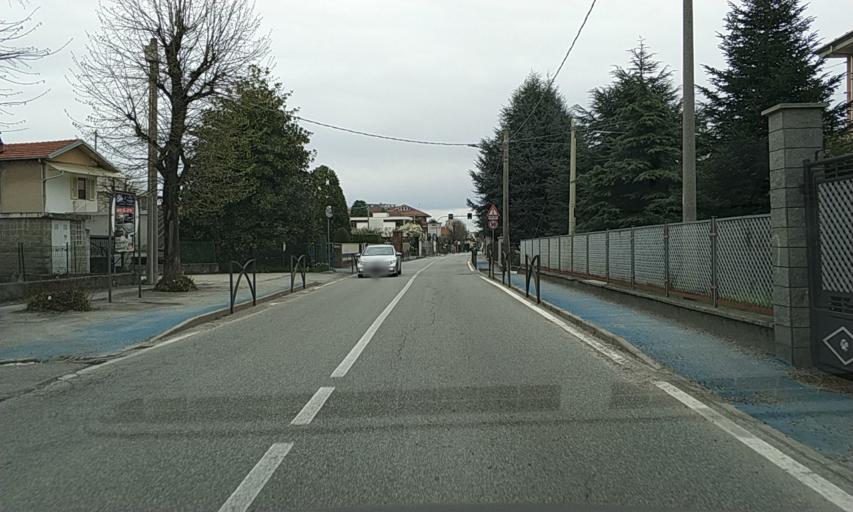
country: IT
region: Piedmont
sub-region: Provincia di Torino
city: Rivarolo Canavese
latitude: 45.3314
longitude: 7.7131
